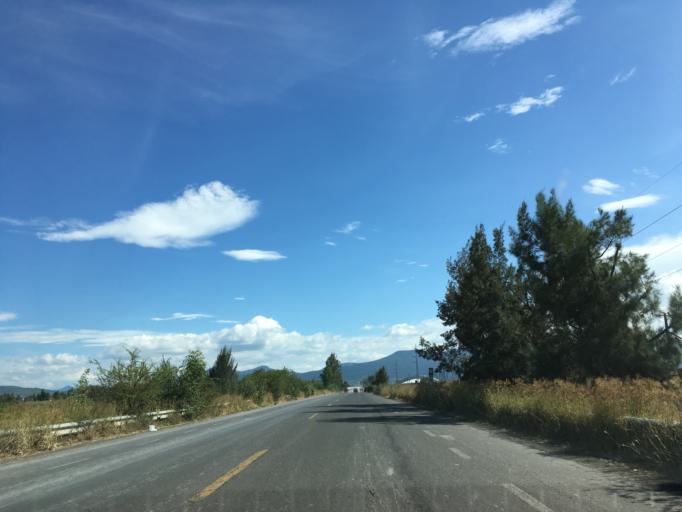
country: MX
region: Michoacan
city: Zacapu
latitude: 19.8480
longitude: -101.7687
